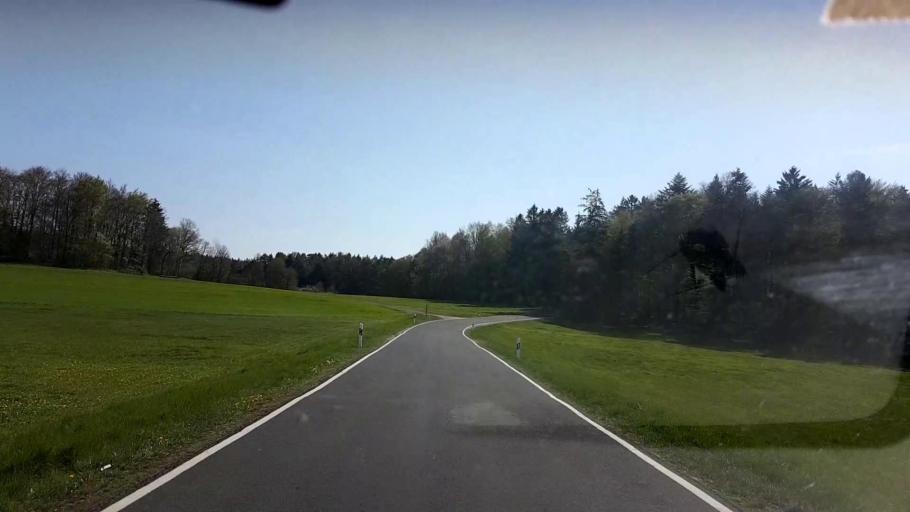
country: DE
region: Bavaria
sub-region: Upper Franconia
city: Pottenstein
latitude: 49.7978
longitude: 11.3986
